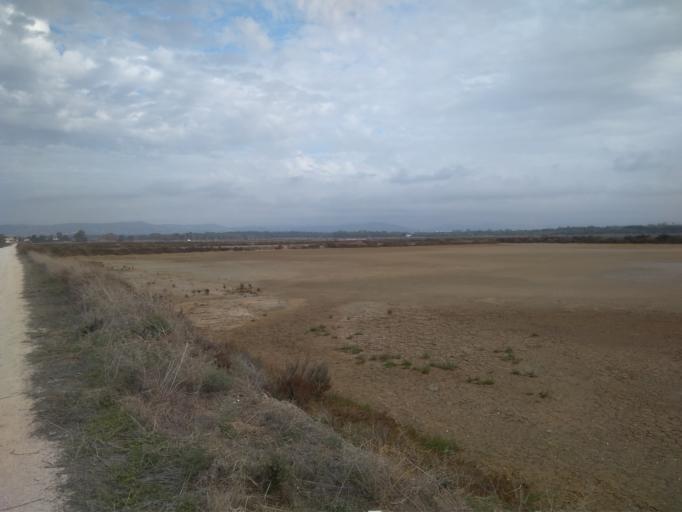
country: PT
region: Faro
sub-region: Faro
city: Faro
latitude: 37.0197
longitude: -7.9969
